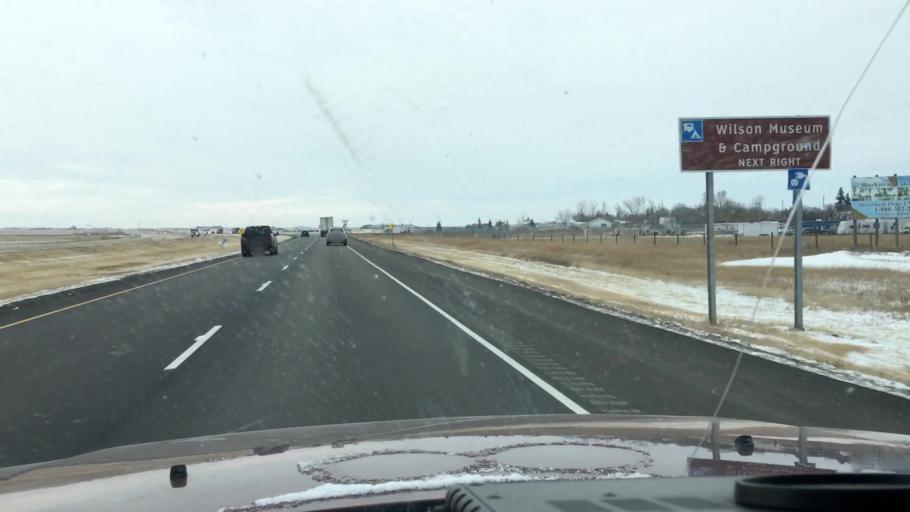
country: CA
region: Saskatchewan
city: Saskatoon
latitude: 51.8151
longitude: -106.4981
